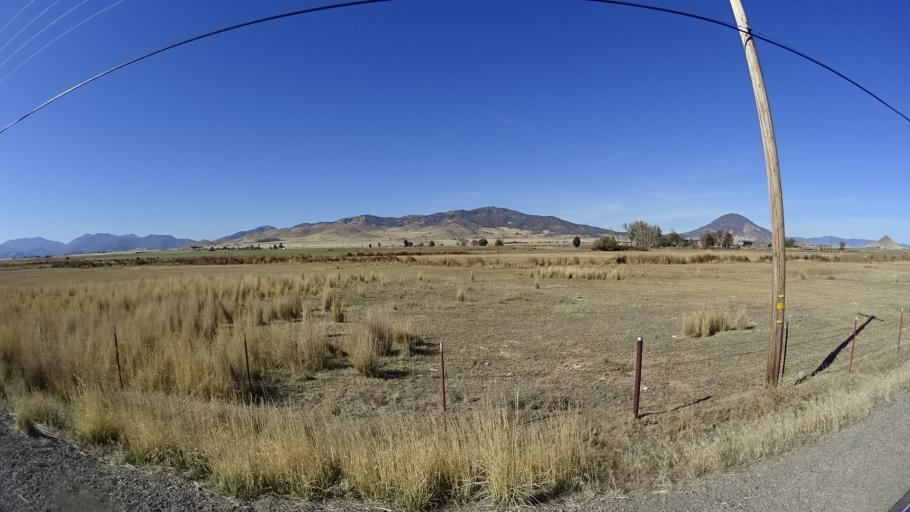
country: US
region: California
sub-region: Siskiyou County
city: Montague
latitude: 41.7679
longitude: -122.4839
